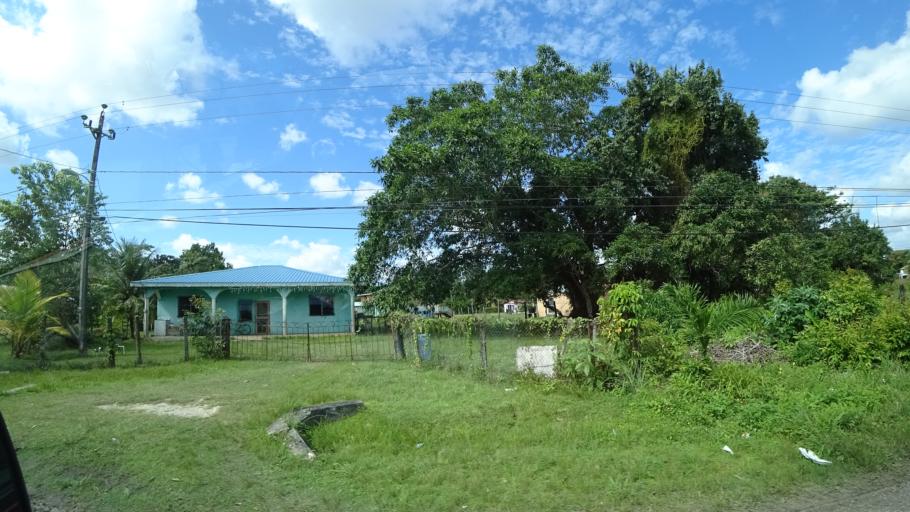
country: BZ
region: Belize
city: Belize City
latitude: 17.5686
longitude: -88.4043
